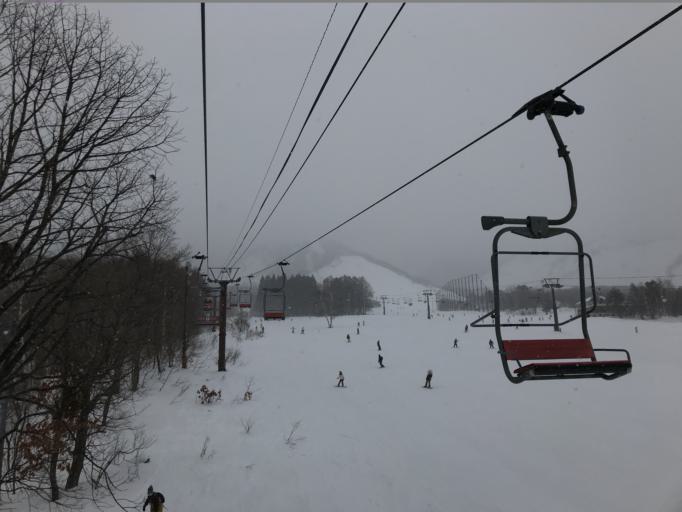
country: JP
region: Nagano
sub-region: Kitaazumi Gun
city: Hakuba
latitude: 36.7514
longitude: 137.8679
